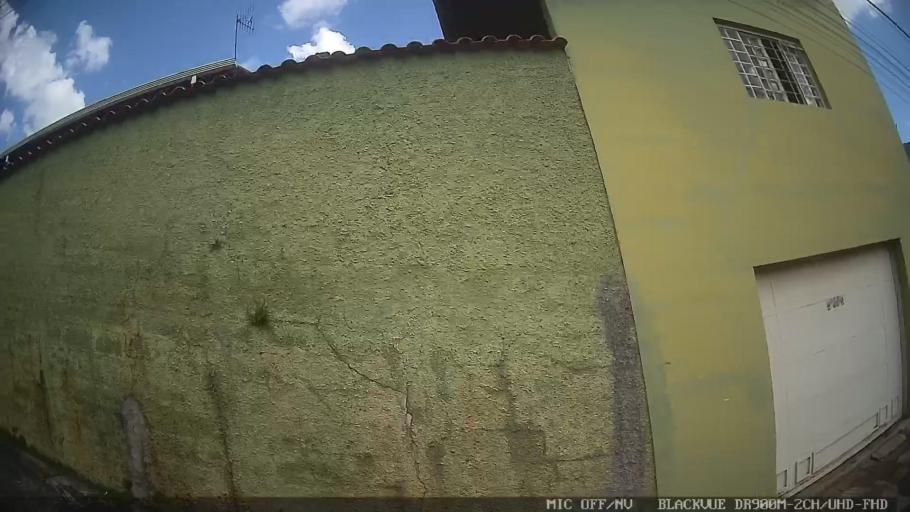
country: BR
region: Minas Gerais
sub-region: Extrema
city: Extrema
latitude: -22.8599
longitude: -46.3201
